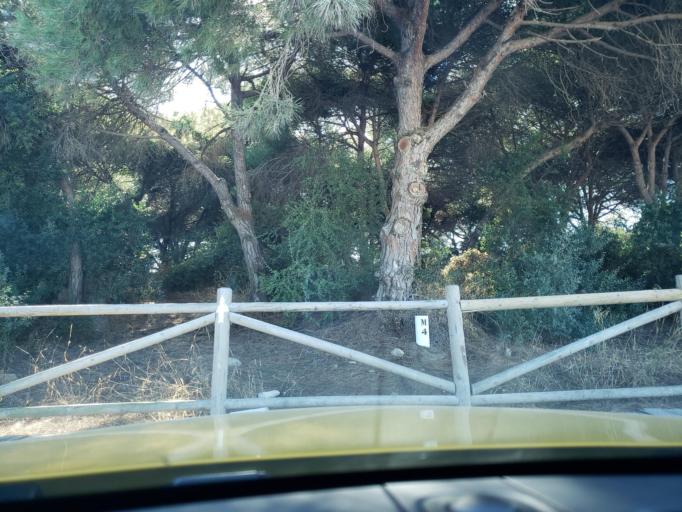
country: ES
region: Andalusia
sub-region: Provincia de Malaga
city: Fuengirola
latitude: 36.4867
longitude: -4.7429
